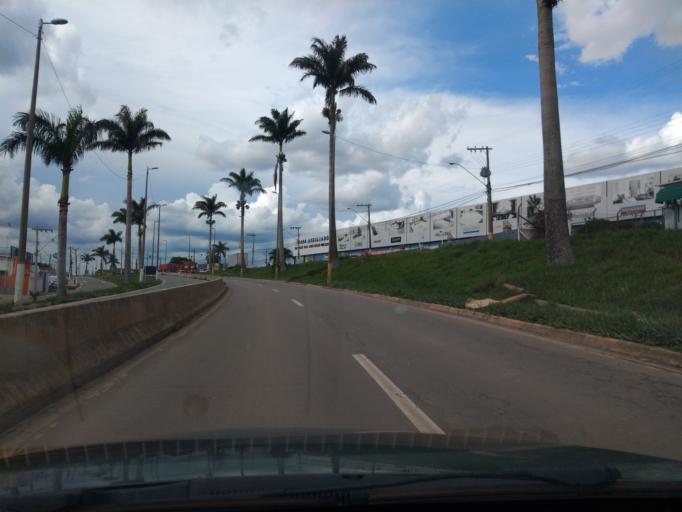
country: BR
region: Minas Gerais
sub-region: Varginha
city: Varginha
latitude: -21.5905
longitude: -45.4374
